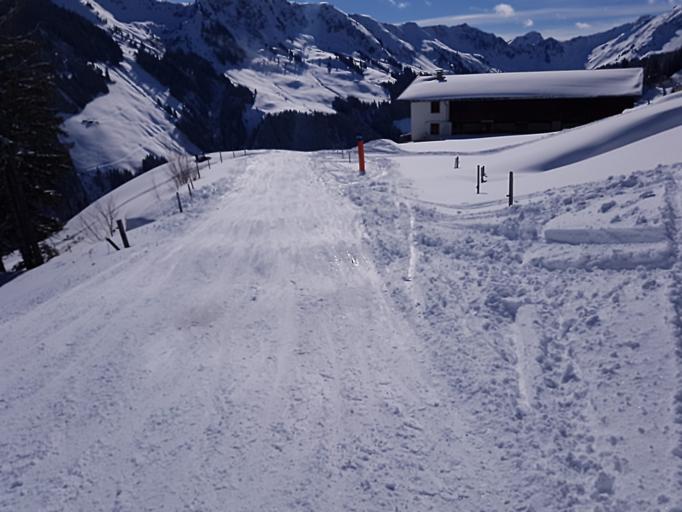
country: AT
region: Tyrol
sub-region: Politischer Bezirk Kitzbuhel
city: Fieberbrunn
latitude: 47.4219
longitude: 12.5657
